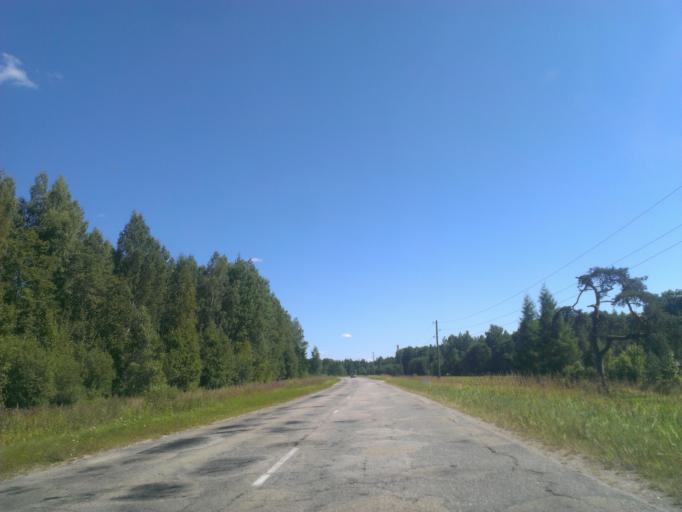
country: LV
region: Incukalns
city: Incukalns
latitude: 57.0231
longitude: 24.7594
